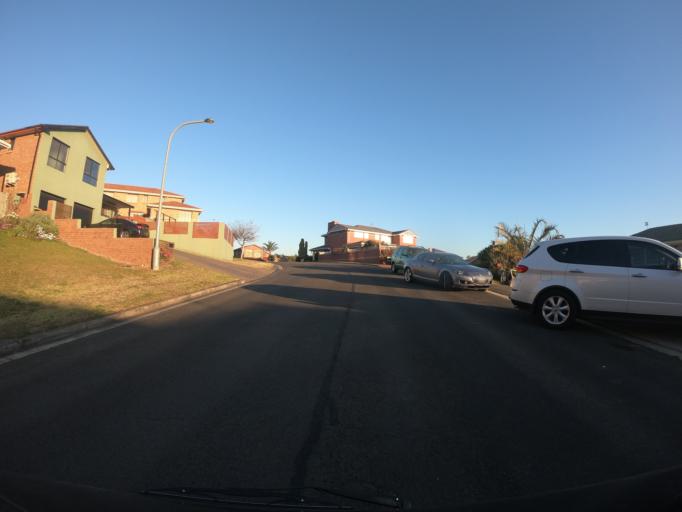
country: AU
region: New South Wales
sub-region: Wollongong
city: Berkeley
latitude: -34.4760
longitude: 150.8591
